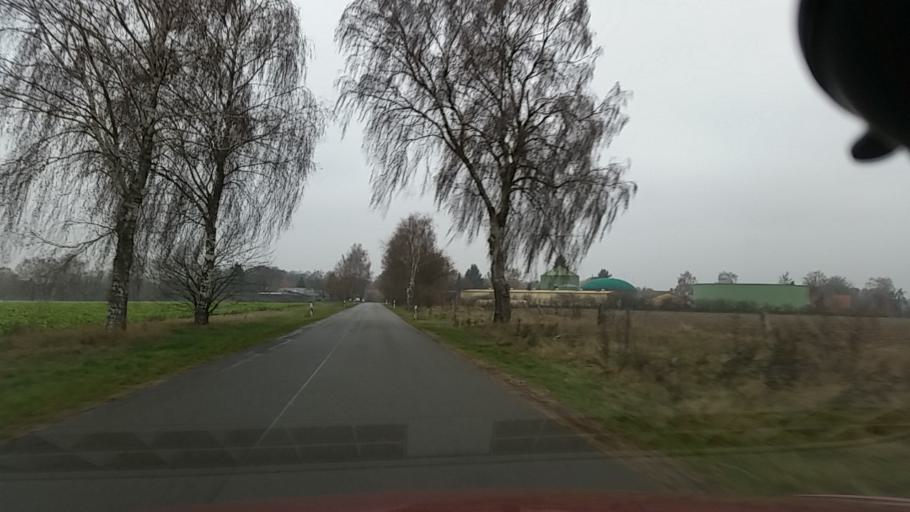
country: DE
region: Lower Saxony
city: Obernholz
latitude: 52.8044
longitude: 10.5517
